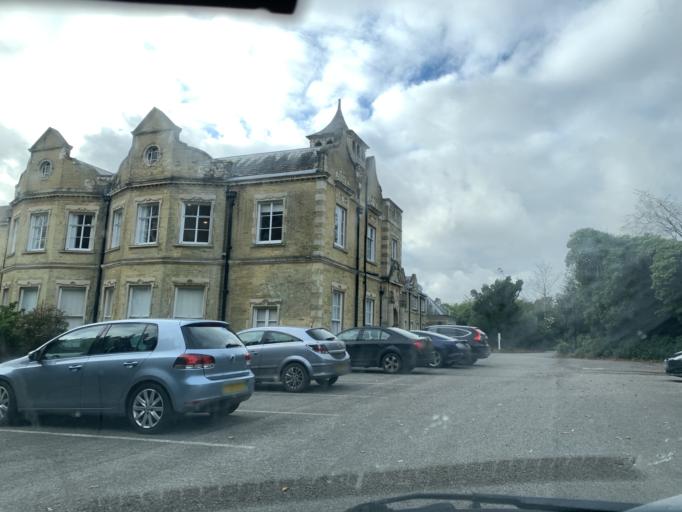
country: GB
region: England
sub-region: Hampshire
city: Cadnam
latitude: 50.9062
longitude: -1.6112
